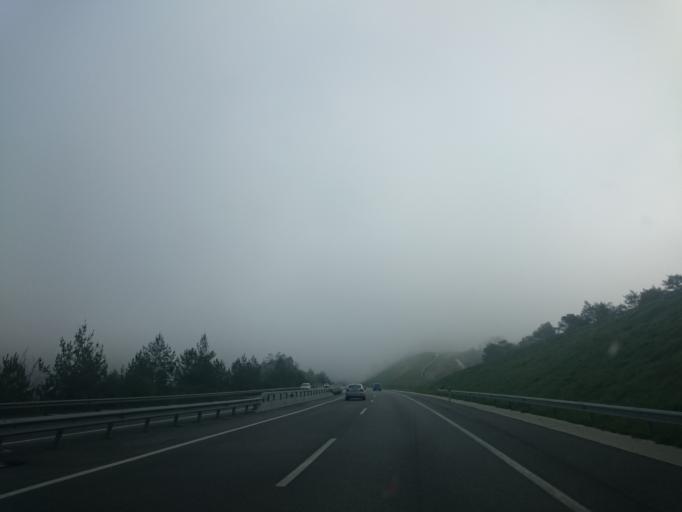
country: ES
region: Catalonia
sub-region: Provincia de Barcelona
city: Muntanyola
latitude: 41.9331
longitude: 2.1680
